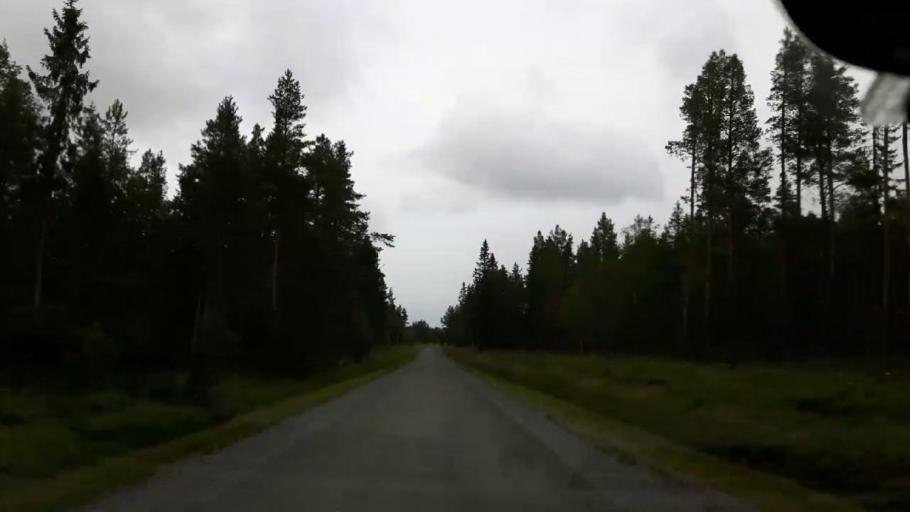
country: SE
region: Jaemtland
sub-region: OEstersunds Kommun
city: Ostersund
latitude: 63.0836
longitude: 14.5550
